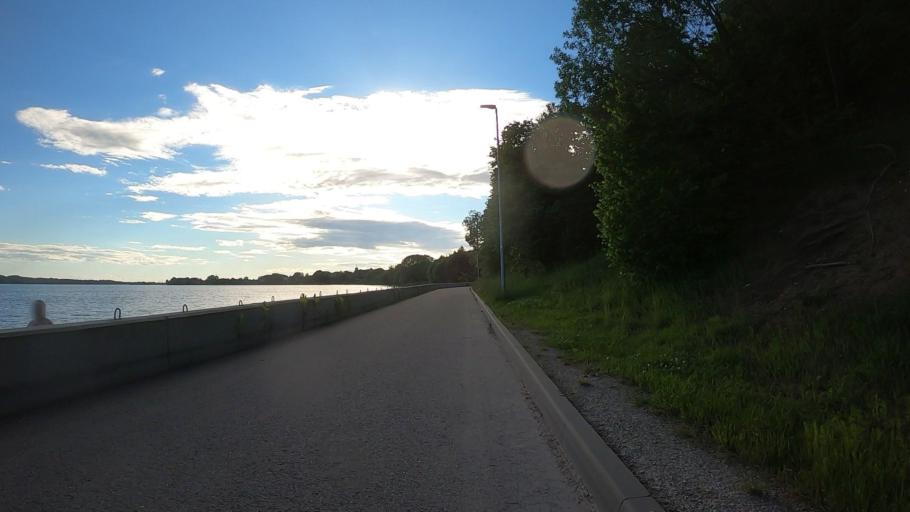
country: LV
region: Ikskile
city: Ikskile
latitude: 56.8433
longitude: 24.4537
